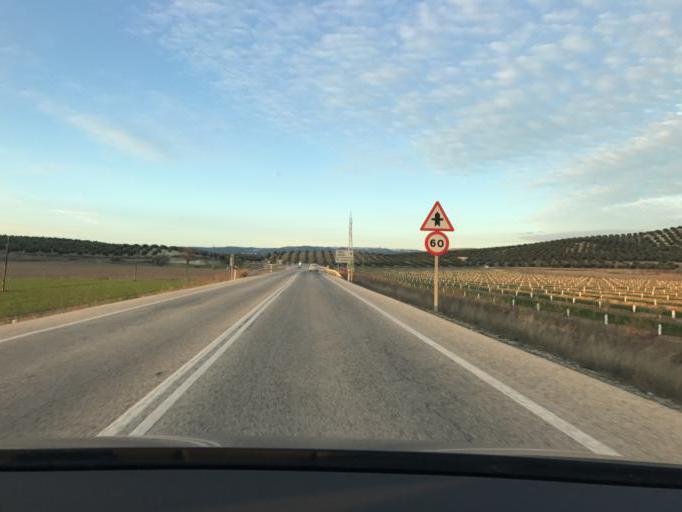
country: ES
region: Andalusia
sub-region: Provincia de Jaen
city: Jodar
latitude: 37.9238
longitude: -3.3528
